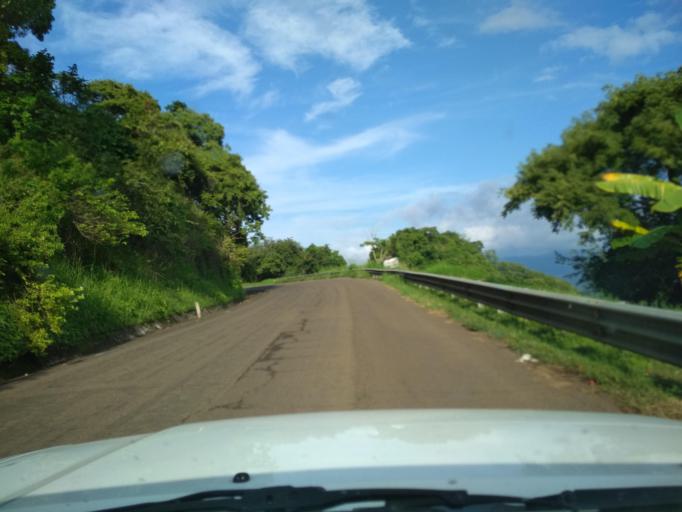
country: MX
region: Veracruz
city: Catemaco
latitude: 18.3859
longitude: -95.1235
